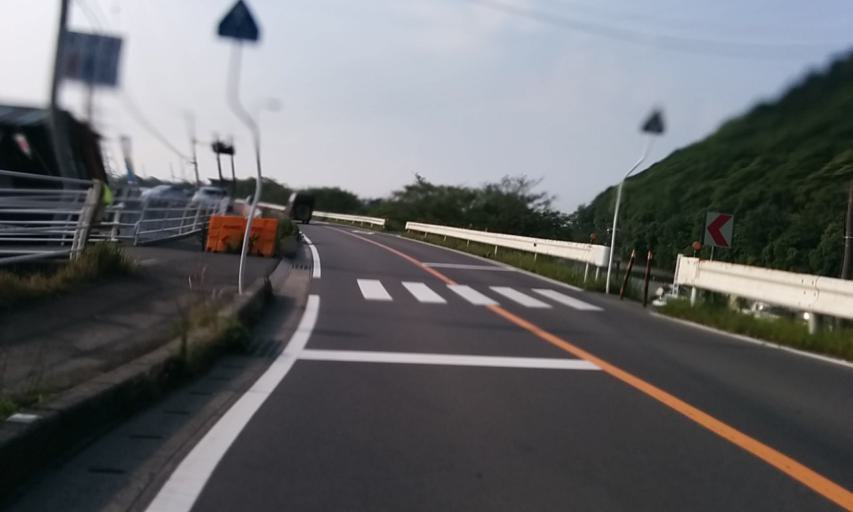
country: JP
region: Ehime
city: Saijo
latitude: 33.8946
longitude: 133.1944
